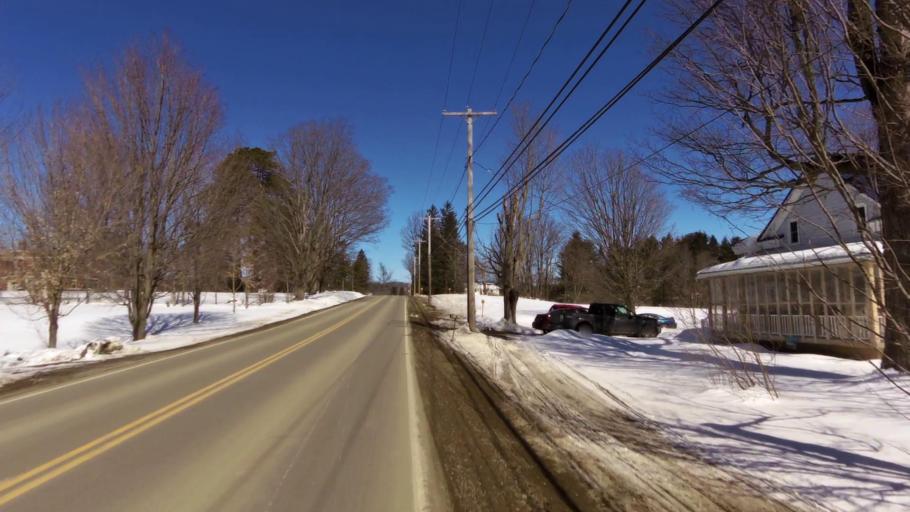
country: US
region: New York
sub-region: Allegany County
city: Houghton
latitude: 42.3838
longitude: -78.2536
